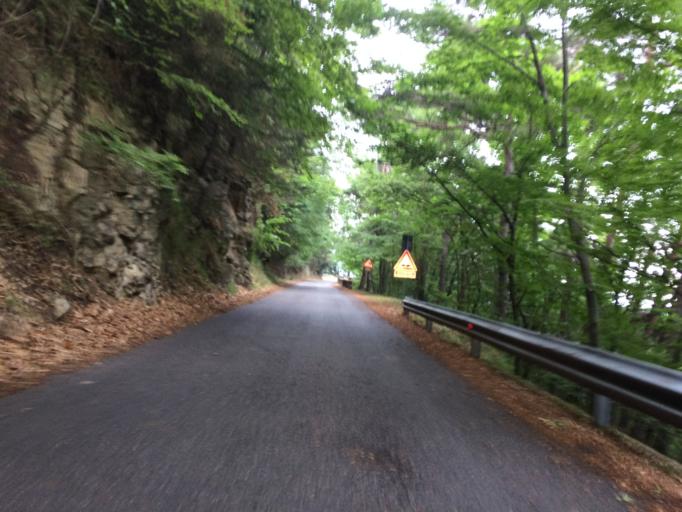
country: IT
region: Liguria
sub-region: Provincia di Imperia
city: Ceriana
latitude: 43.8759
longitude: 7.7432
